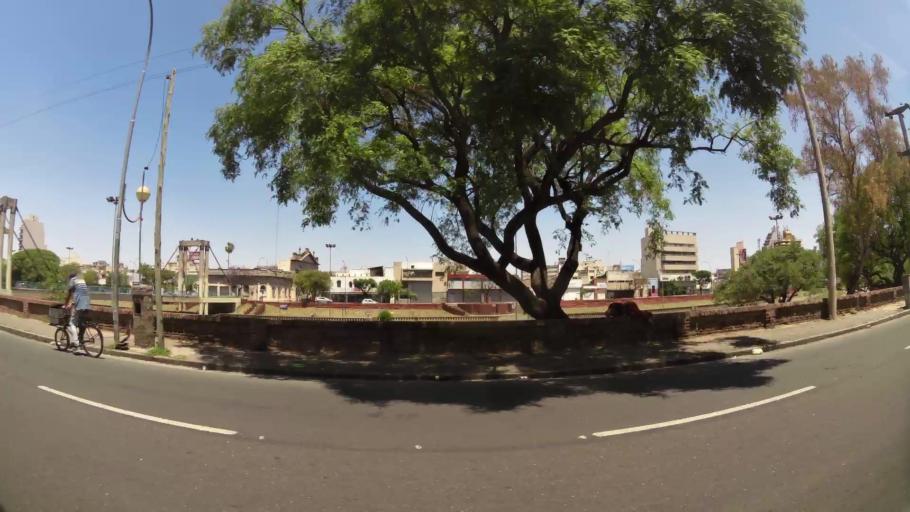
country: AR
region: Cordoba
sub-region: Departamento de Capital
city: Cordoba
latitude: -31.4053
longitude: -64.1801
